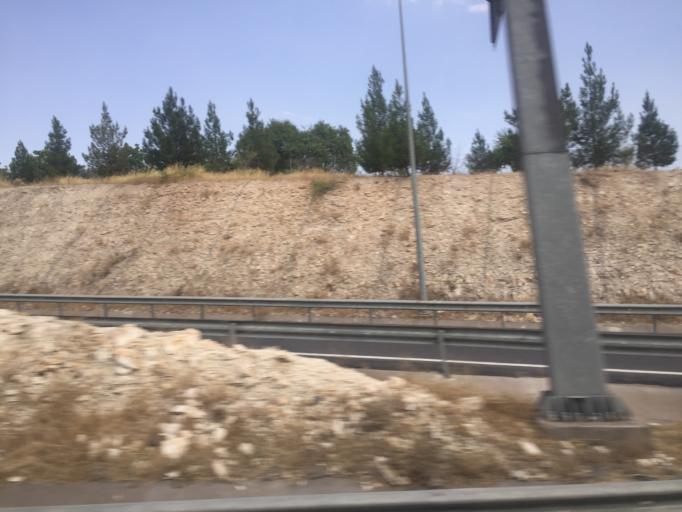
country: TR
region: Sanliurfa
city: Akziyaret
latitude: 37.2679
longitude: 38.8014
